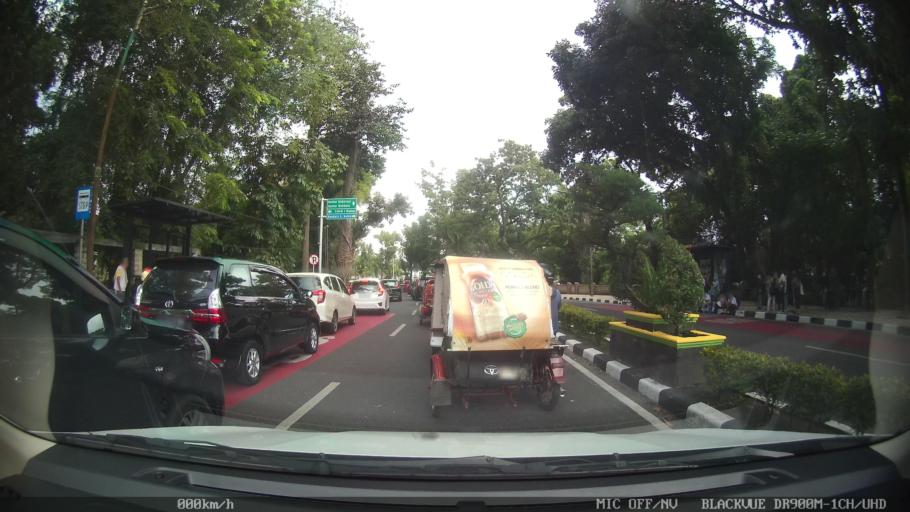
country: ID
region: North Sumatra
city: Medan
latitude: 3.5762
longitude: 98.6687
